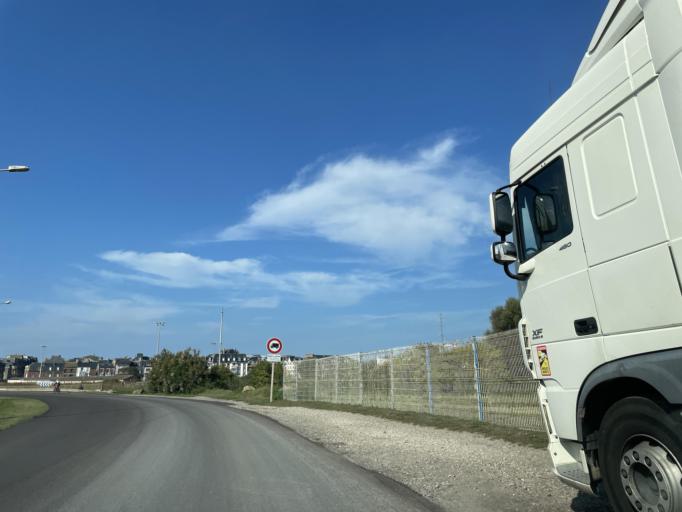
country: FR
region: Picardie
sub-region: Departement de la Somme
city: Mers-les-Bains
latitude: 50.0628
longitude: 1.3851
